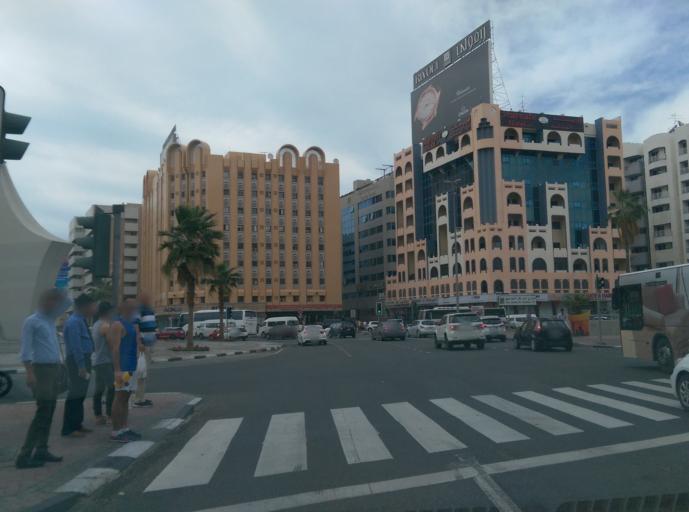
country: AE
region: Ash Shariqah
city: Sharjah
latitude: 25.2586
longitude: 55.3270
